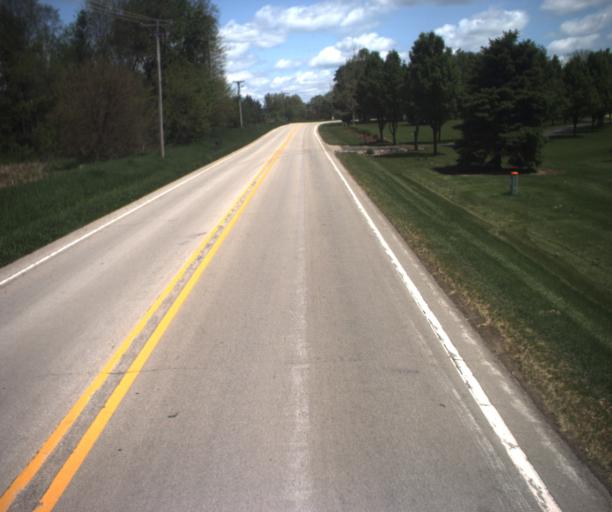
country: US
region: Illinois
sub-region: Kane County
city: North Aurora
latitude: 41.8526
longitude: -88.3972
